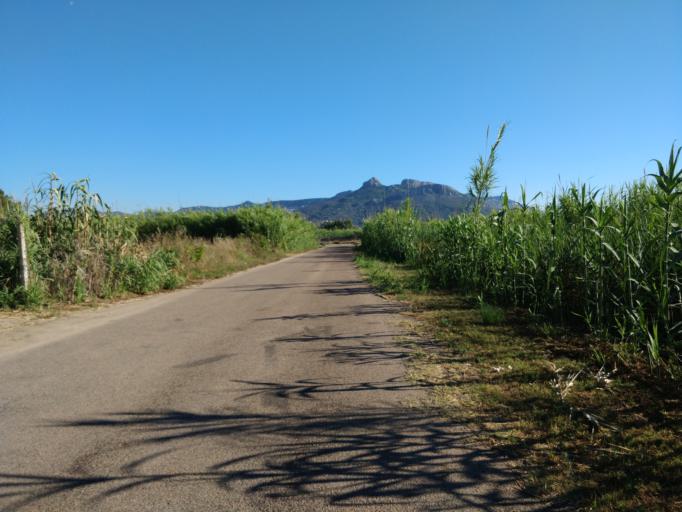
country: IT
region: Sardinia
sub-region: Provincia di Ogliastra
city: Lotzorai
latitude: 39.9595
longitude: 9.6774
